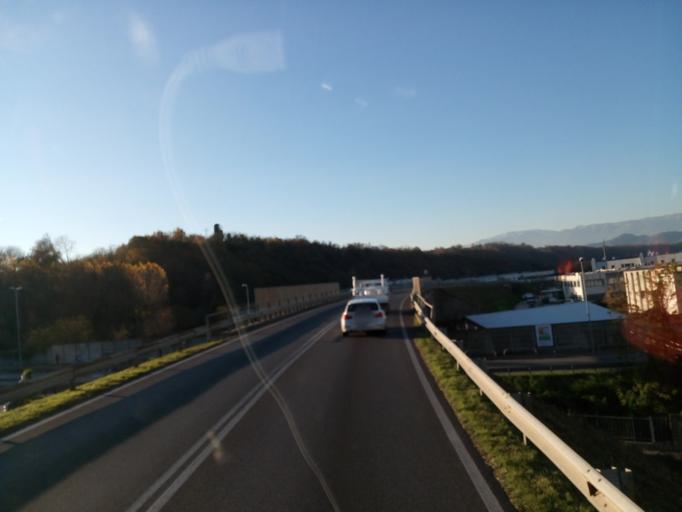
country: IT
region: Veneto
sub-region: Provincia di Treviso
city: Montebelluna
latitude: 45.7832
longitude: 12.0531
